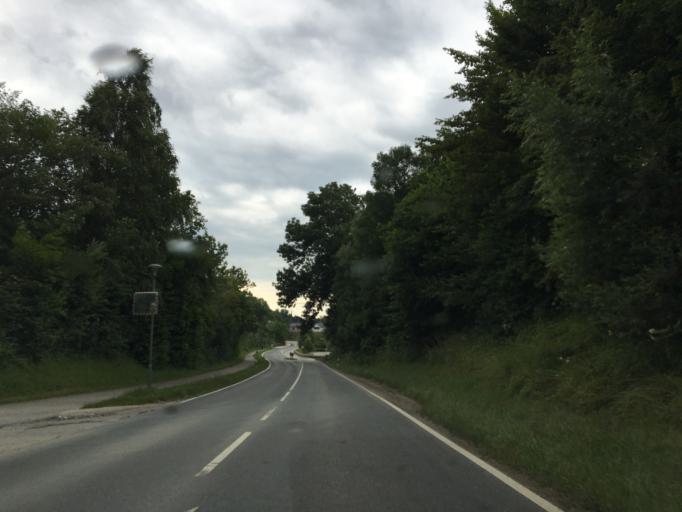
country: DE
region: Bavaria
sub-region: Upper Bavaria
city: Flintsbach
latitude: 47.7296
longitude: 12.1145
